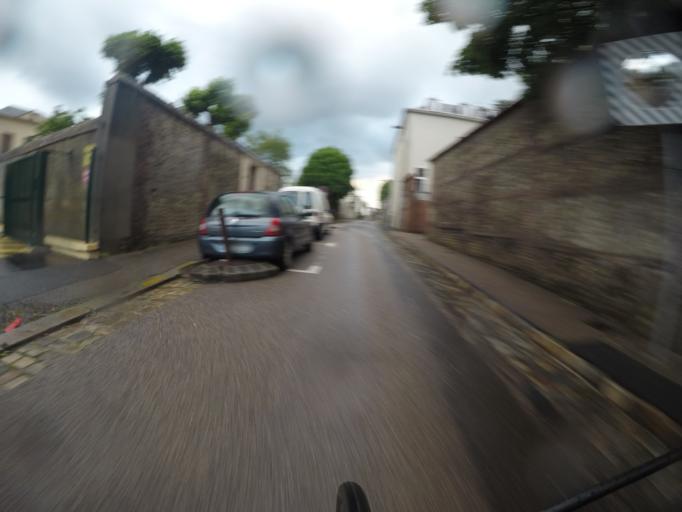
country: FR
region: Haute-Normandie
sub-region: Departement de la Seine-Maritime
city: Rouen
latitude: 49.4525
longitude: 1.0958
